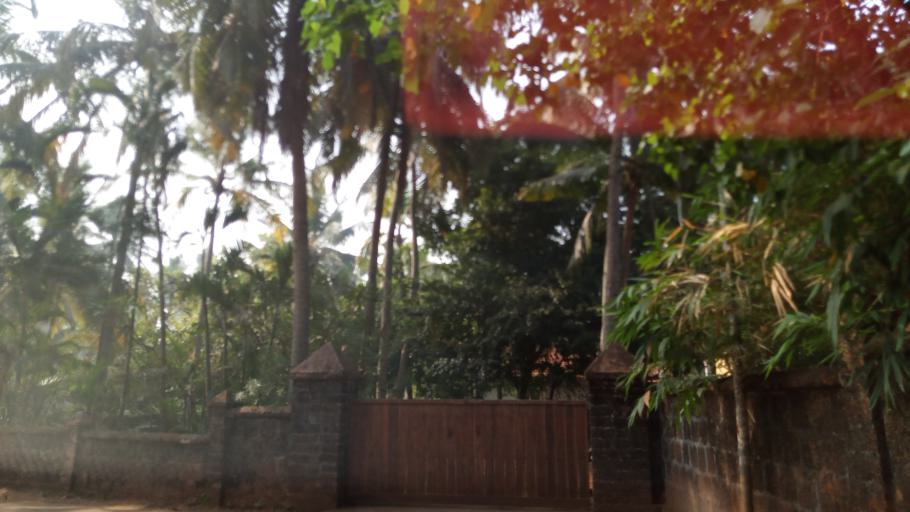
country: IN
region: Goa
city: Calangute
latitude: 15.5414
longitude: 73.7590
